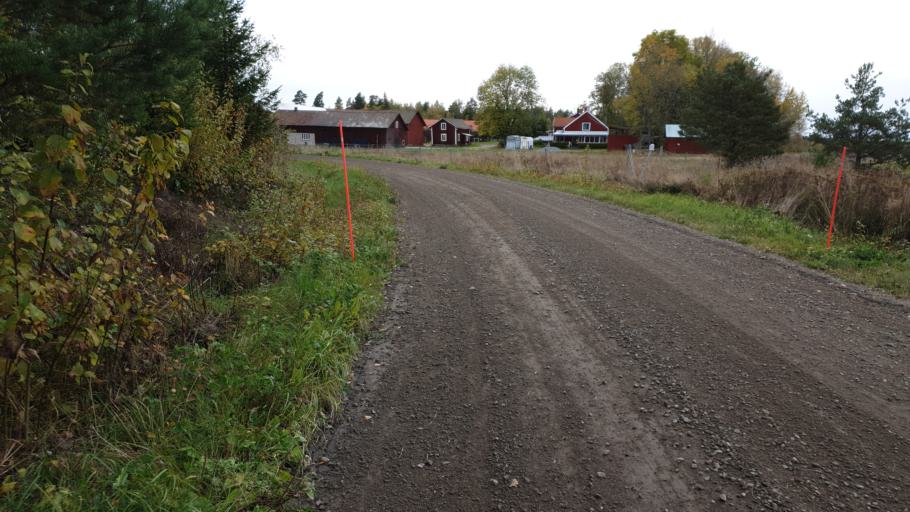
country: SE
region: Vaestmanland
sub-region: Sala Kommun
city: Sala
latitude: 59.8171
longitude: 16.6575
